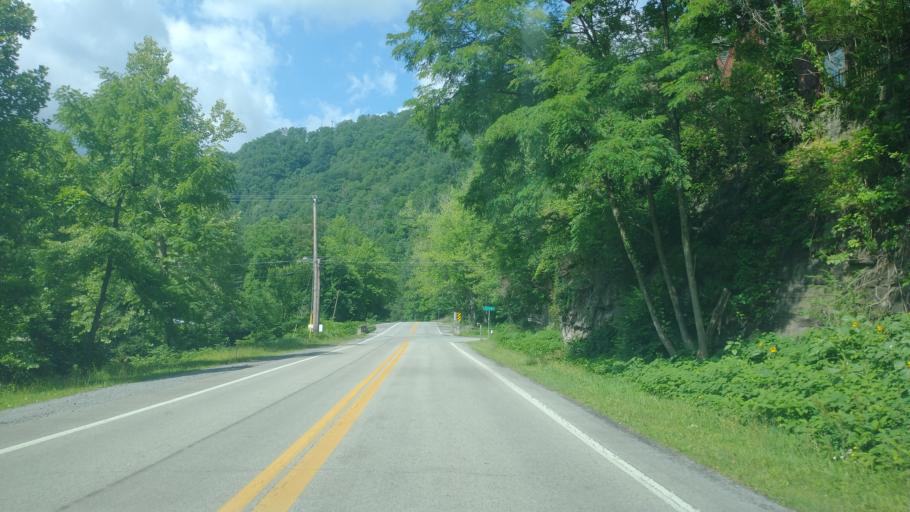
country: US
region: West Virginia
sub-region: McDowell County
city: Welch
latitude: 37.4301
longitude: -81.5074
